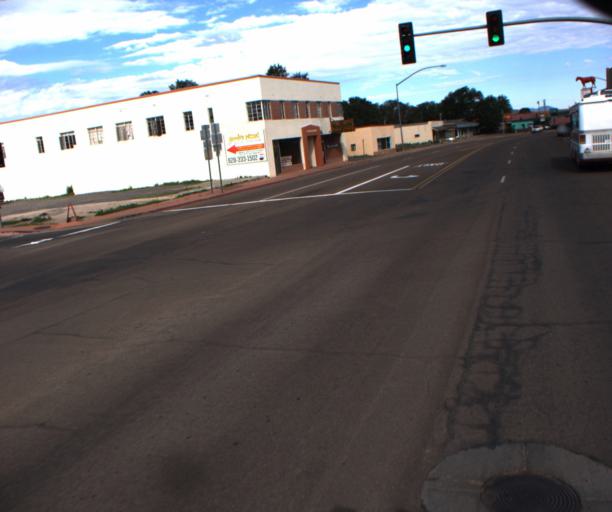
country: US
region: Arizona
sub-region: Apache County
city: Springerville
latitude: 34.1336
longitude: -109.2856
